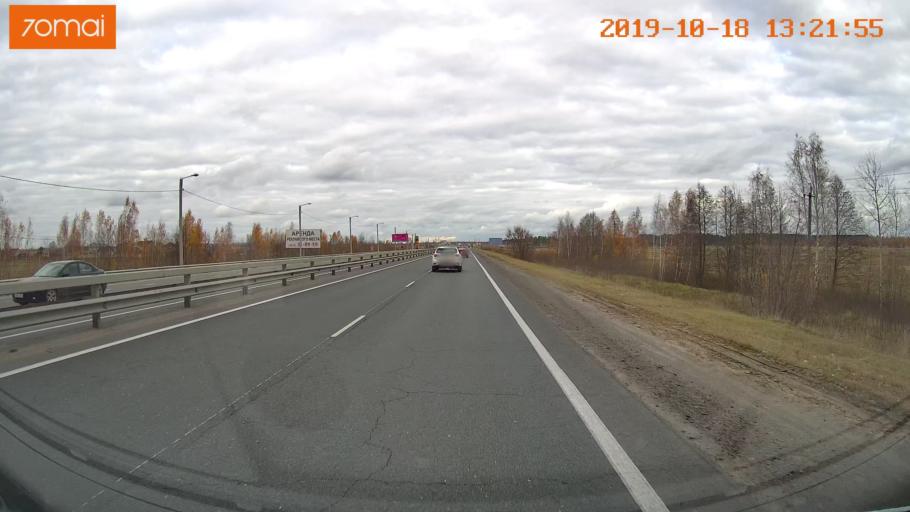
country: RU
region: Rjazan
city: Polyany
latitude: 54.7023
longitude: 39.8431
